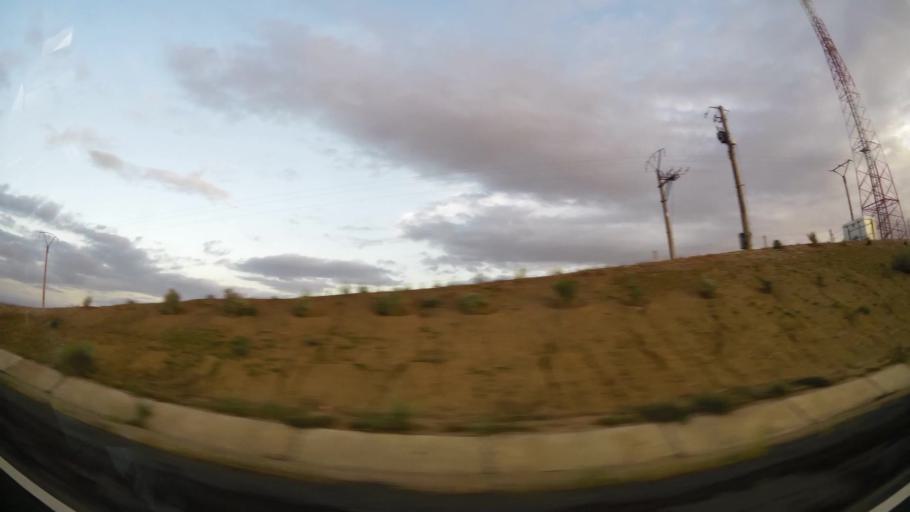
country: MA
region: Oriental
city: Taourirt
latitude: 34.5478
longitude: -2.8965
